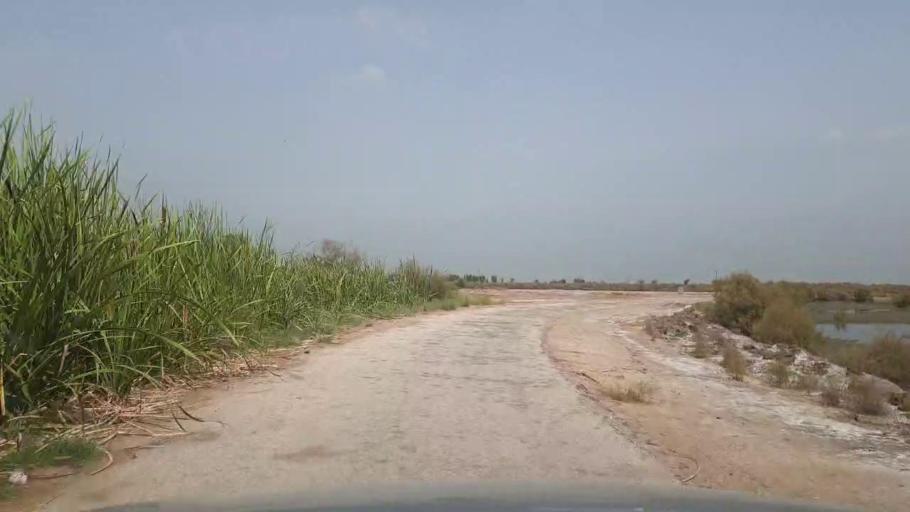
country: PK
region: Sindh
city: Garhi Yasin
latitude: 27.9512
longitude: 68.3652
